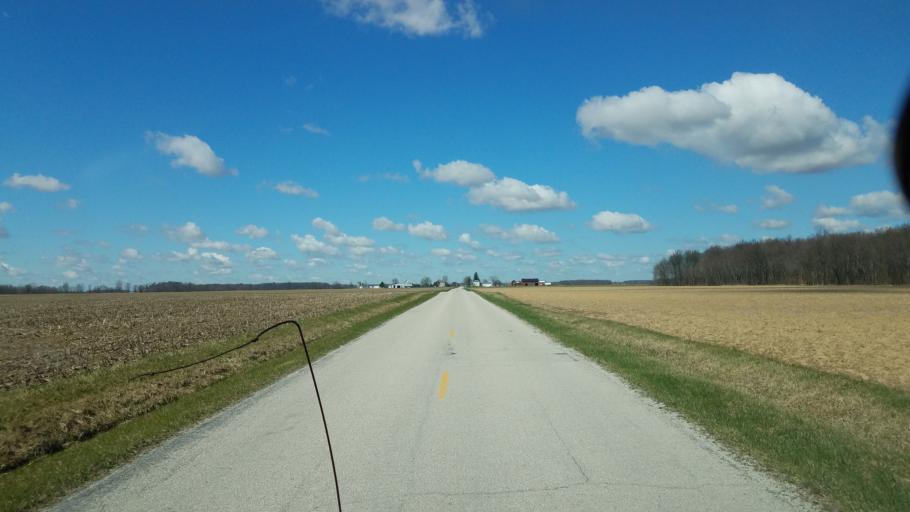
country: US
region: Ohio
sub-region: Huron County
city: Willard
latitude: 41.0229
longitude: -82.9119
